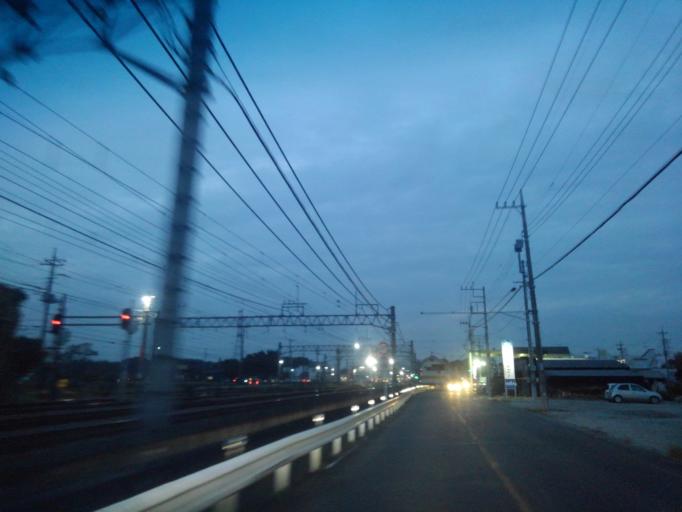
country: JP
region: Saitama
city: Tokorozawa
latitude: 35.8184
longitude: 139.4430
